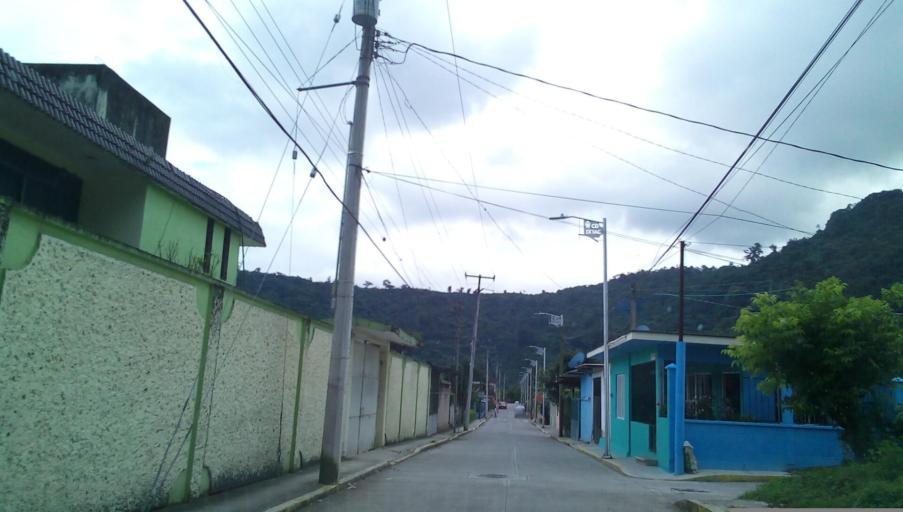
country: MX
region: Veracruz
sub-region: Ixtaczoquitlan
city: Buenavista
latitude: 18.8929
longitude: -97.0397
